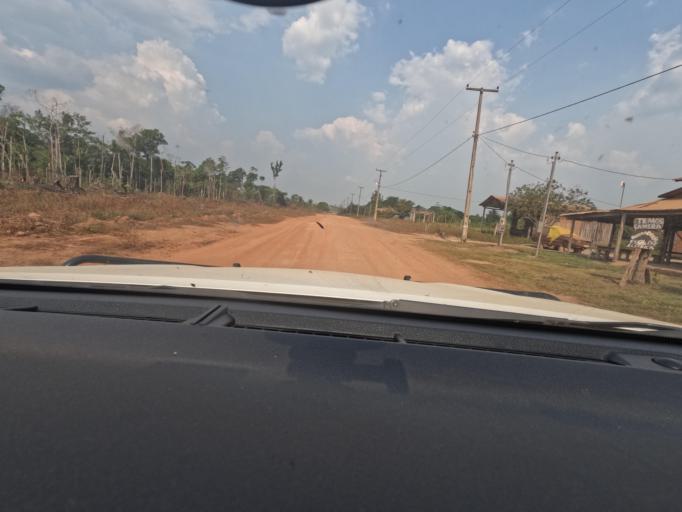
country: BR
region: Rondonia
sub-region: Porto Velho
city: Porto Velho
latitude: -8.6831
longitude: -63.1868
